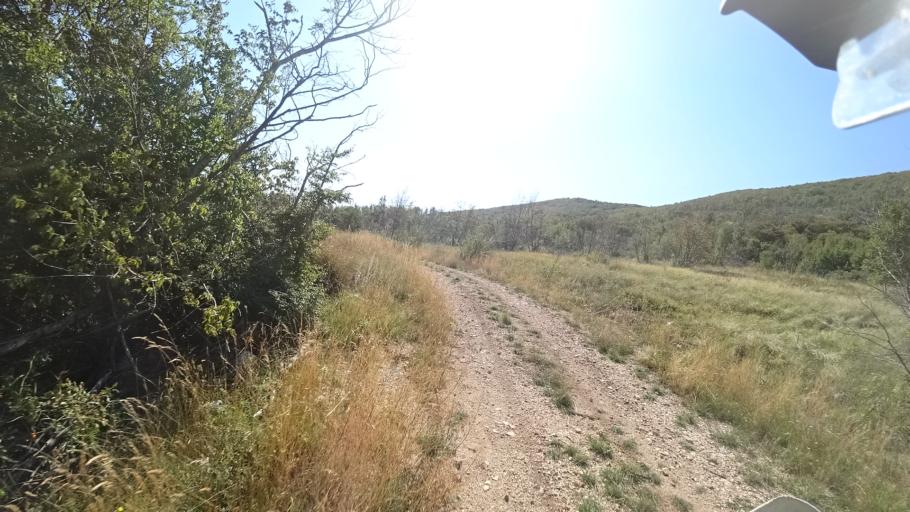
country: HR
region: Sibensko-Kniniska
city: Drnis
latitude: 43.9366
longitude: 16.1608
